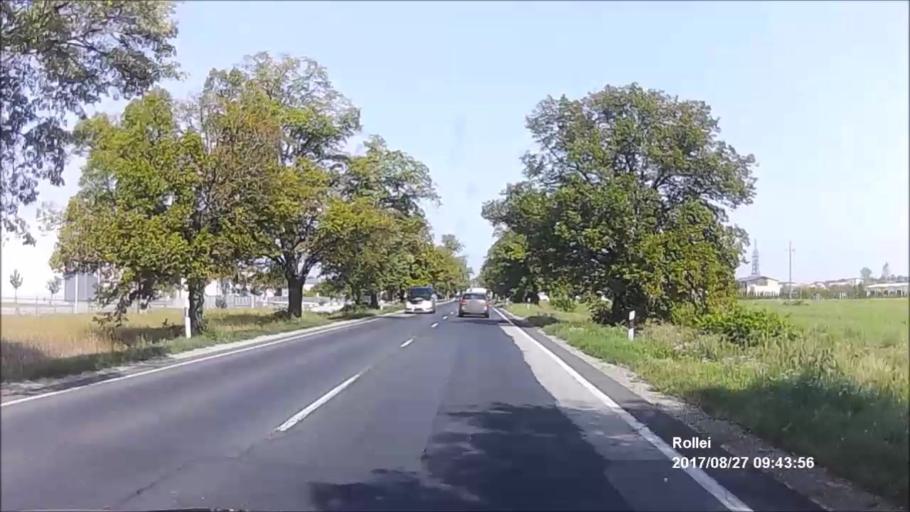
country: HU
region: Gyor-Moson-Sopron
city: Sopron
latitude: 47.6645
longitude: 16.6220
